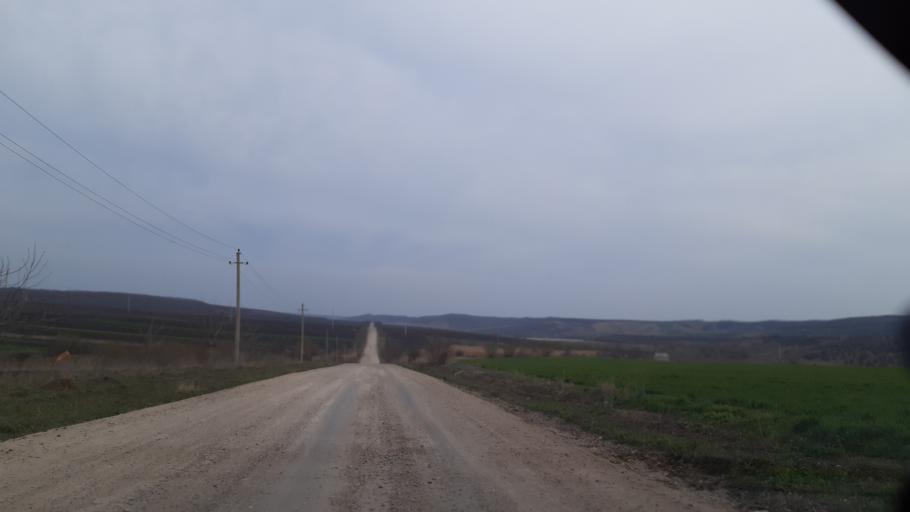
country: MD
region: Soldanesti
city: Soldanesti
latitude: 47.7065
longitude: 28.7122
